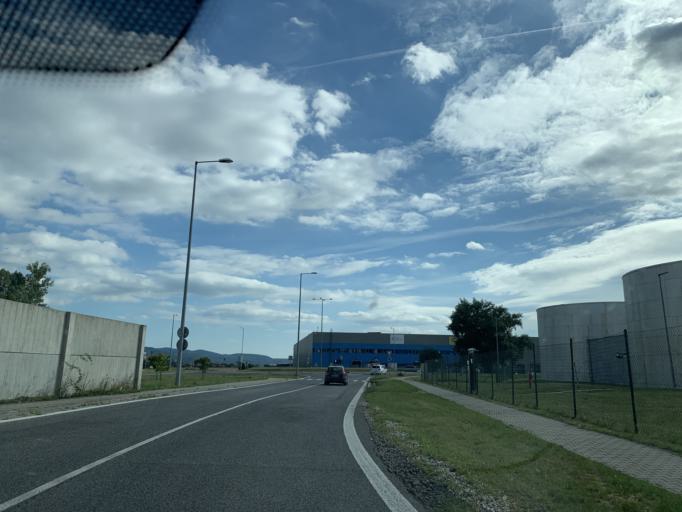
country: SK
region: Trenciansky
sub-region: Okres Nove Mesto nad Vahom
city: Nove Mesto nad Vahom
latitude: 48.7623
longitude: 17.8781
